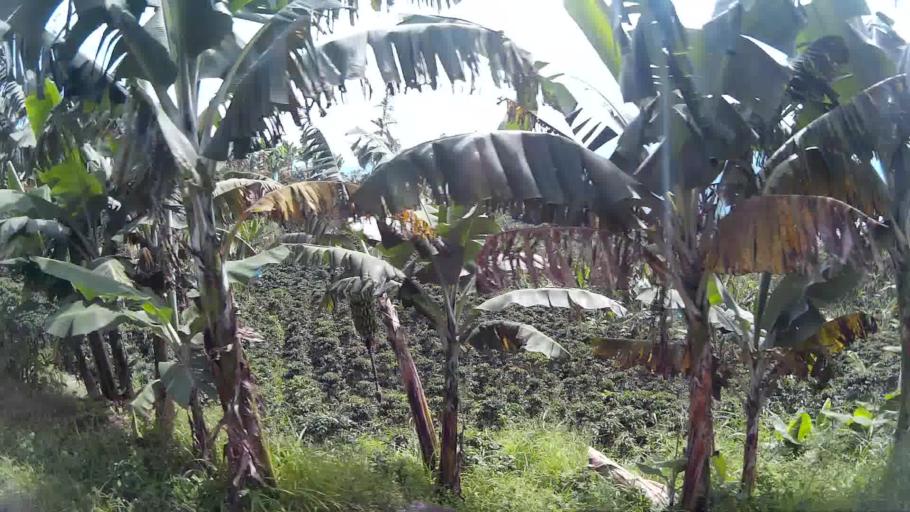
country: CO
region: Caldas
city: Belalcazar
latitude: 4.9695
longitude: -75.8211
